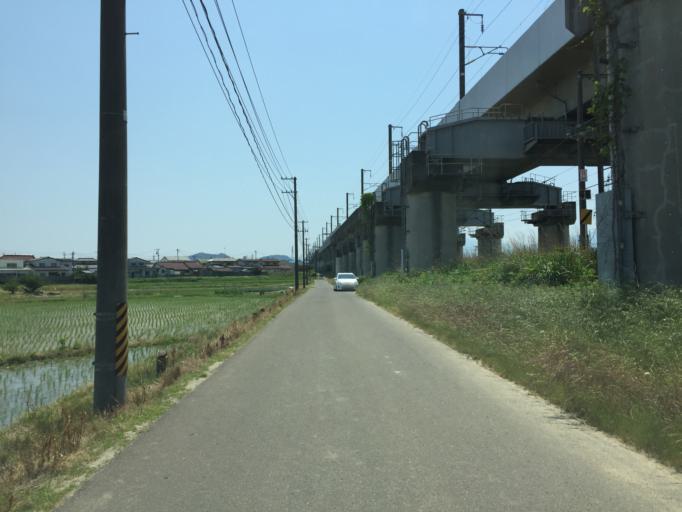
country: JP
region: Fukushima
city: Hobaramachi
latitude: 37.8287
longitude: 140.4970
